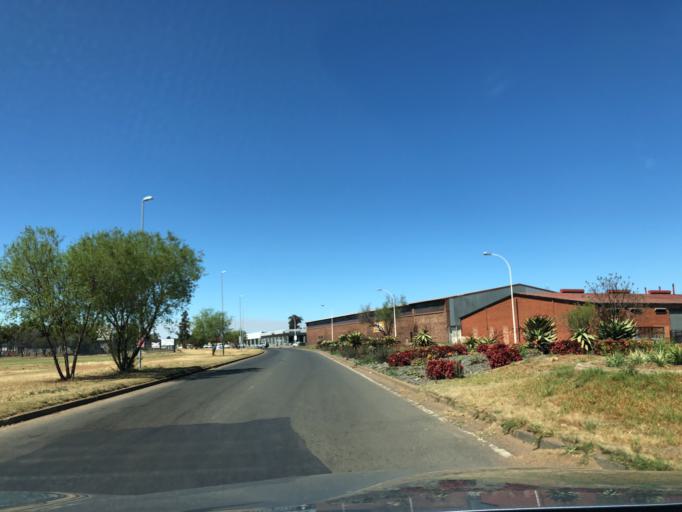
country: ZA
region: KwaZulu-Natal
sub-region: Amajuba District Municipality
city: Newcastle
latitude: -27.7510
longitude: 29.9379
